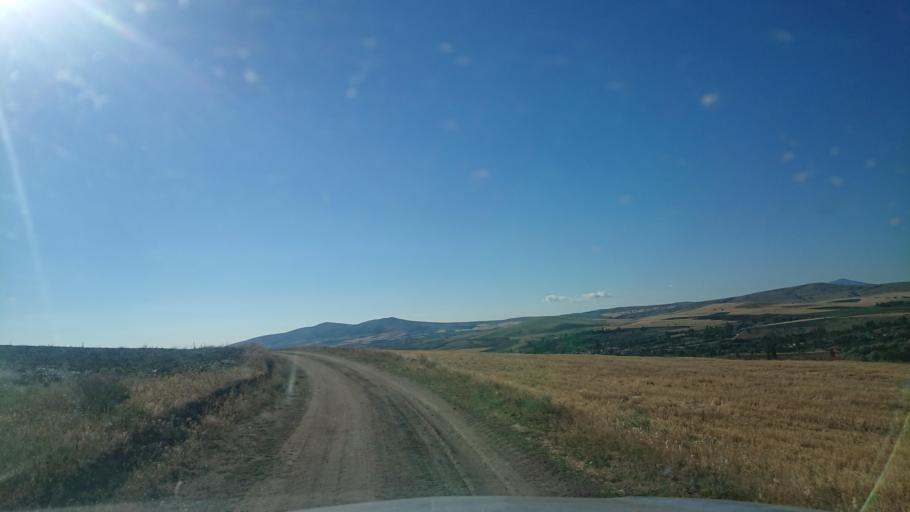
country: TR
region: Aksaray
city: Agacoren
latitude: 38.8292
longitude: 33.9448
